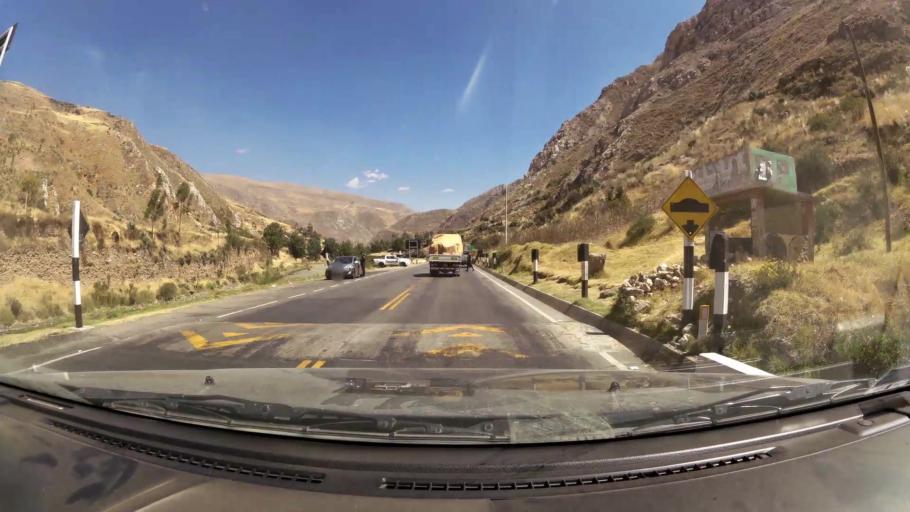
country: PE
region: Junin
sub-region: Provincia de Jauja
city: Parco
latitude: -11.7924
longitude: -75.5873
